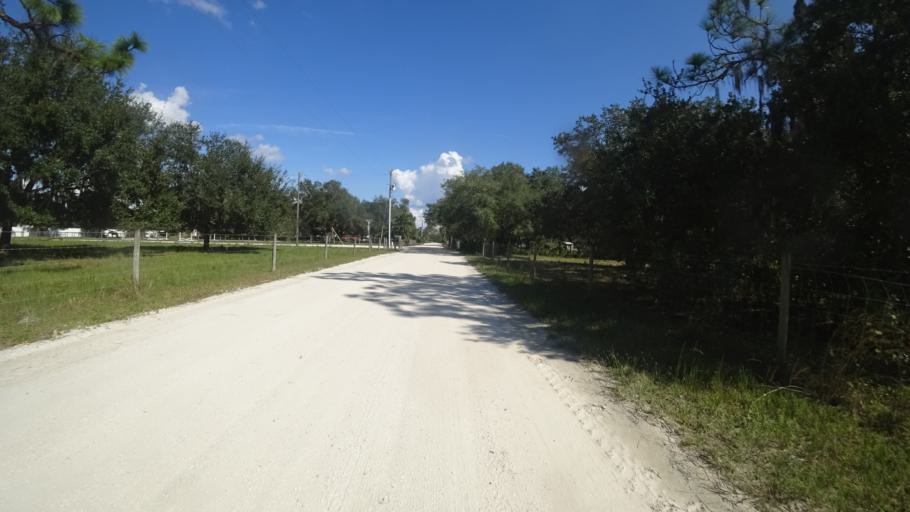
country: US
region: Florida
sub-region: Sarasota County
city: The Meadows
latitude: 27.4525
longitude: -82.2915
